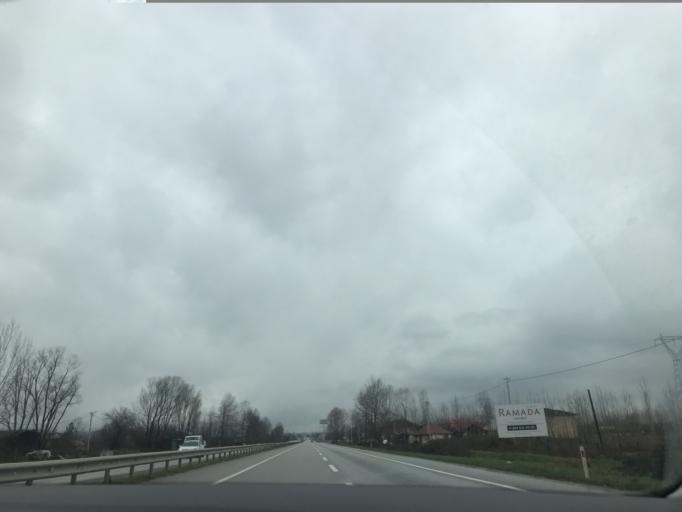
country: TR
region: Sakarya
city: Akyazi
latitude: 40.7723
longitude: 30.6370
